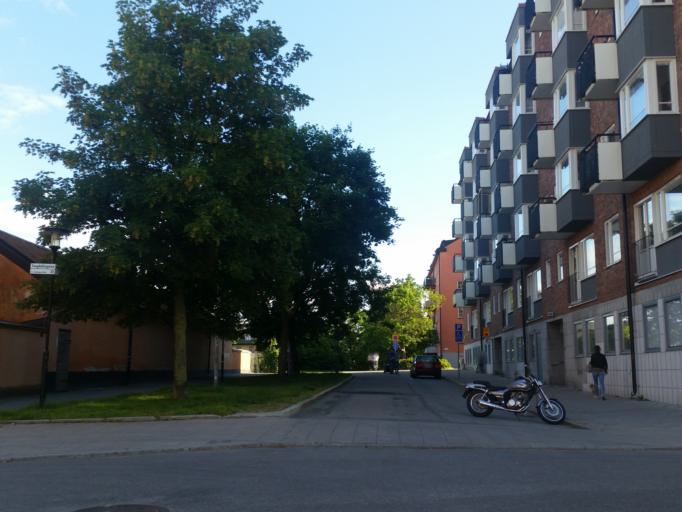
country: SE
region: Stockholm
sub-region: Stockholms Kommun
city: OEstermalm
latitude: 59.3100
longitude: 18.0954
